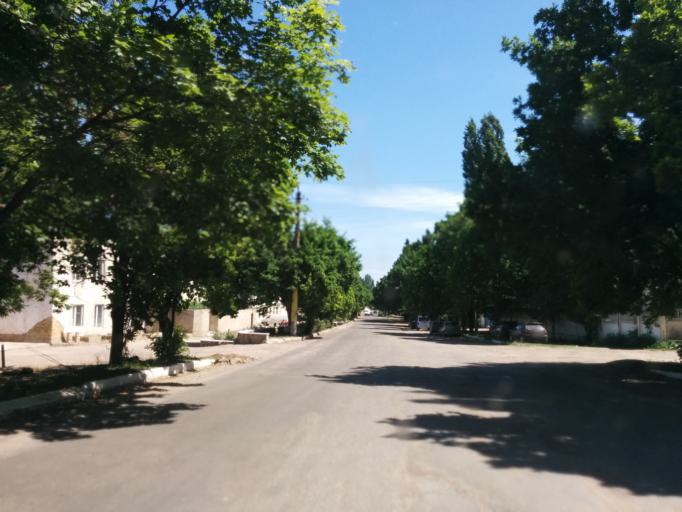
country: MD
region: Raionul Soroca
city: Soroca
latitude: 48.1622
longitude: 28.2838
